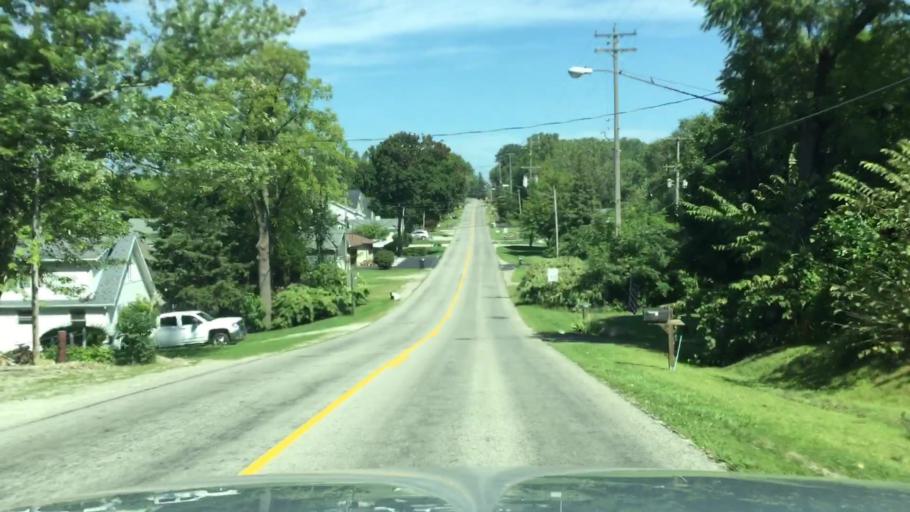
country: US
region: Michigan
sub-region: Lenawee County
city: Manitou Beach-Devils Lake
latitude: 41.9975
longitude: -84.2808
